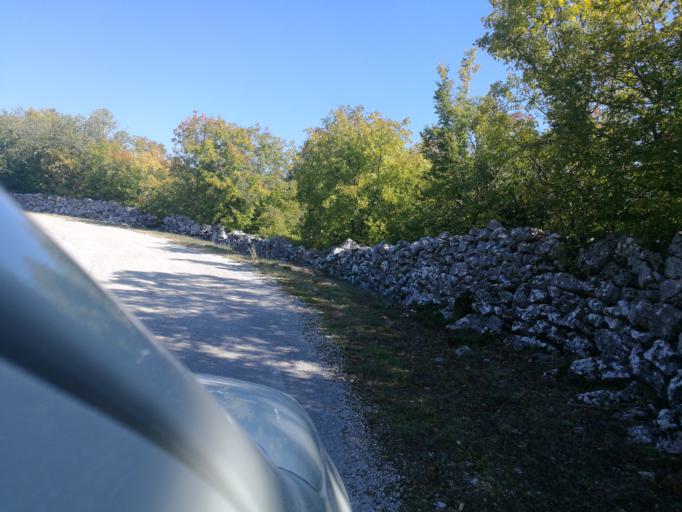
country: HR
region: Splitsko-Dalmatinska
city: Trilj
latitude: 43.5415
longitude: 16.7332
